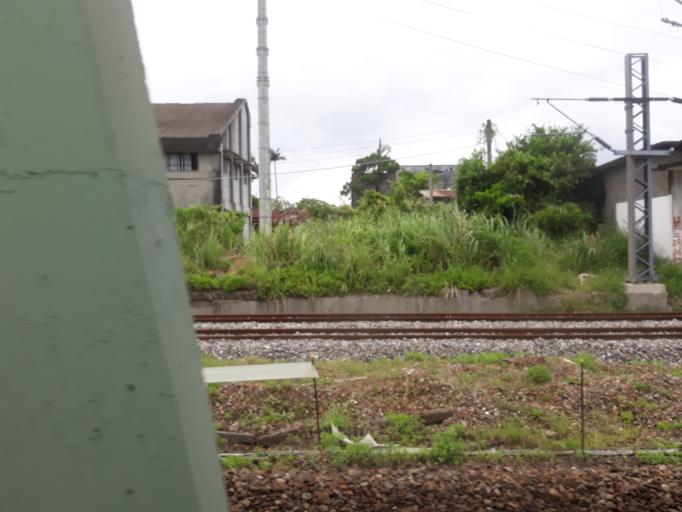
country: TW
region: Taiwan
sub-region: Yilan
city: Yilan
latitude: 24.6941
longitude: 121.7751
